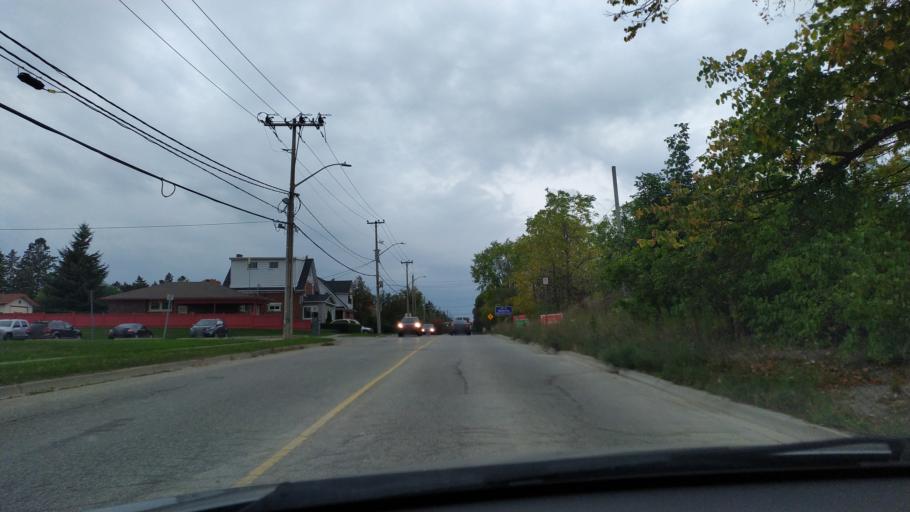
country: CA
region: Ontario
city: Waterloo
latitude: 43.4836
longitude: -80.4860
